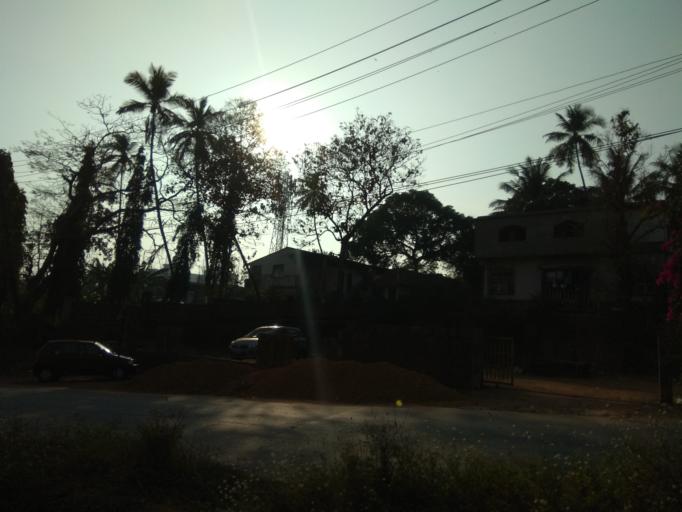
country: IN
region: Karnataka
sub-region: Dakshina Kannada
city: Mangalore
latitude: 12.9084
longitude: 74.8506
